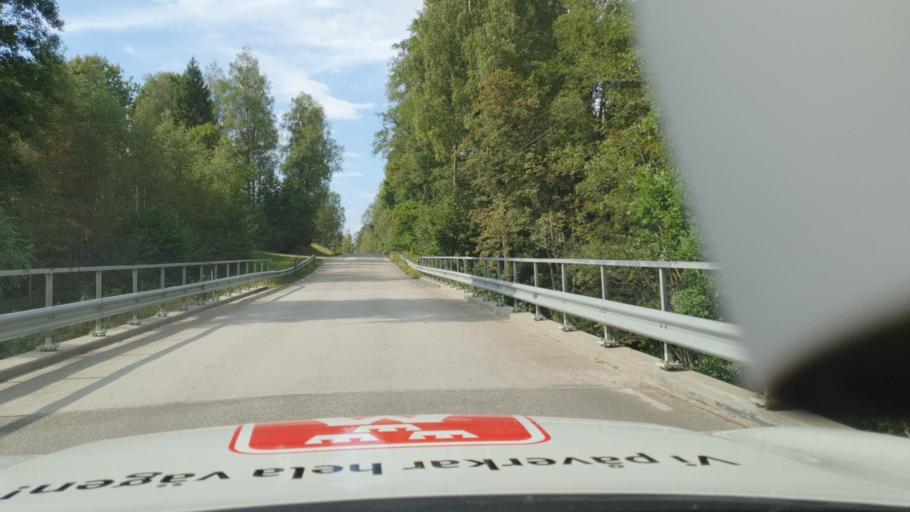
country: SE
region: Vaestra Goetaland
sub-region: Marks Kommun
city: Kinna
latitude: 57.3880
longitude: 12.7206
